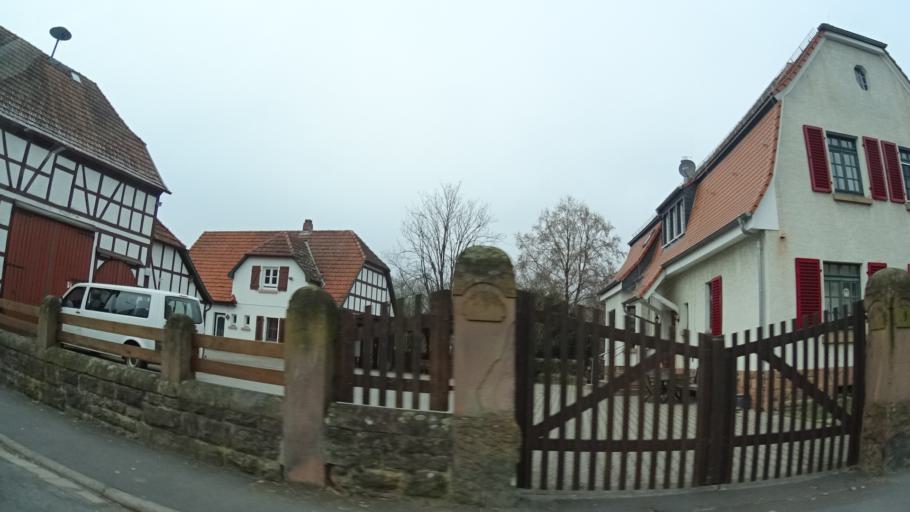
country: DE
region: Hesse
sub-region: Regierungsbezirk Darmstadt
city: Steinau an der Strasse
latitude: 50.2588
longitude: 9.5186
